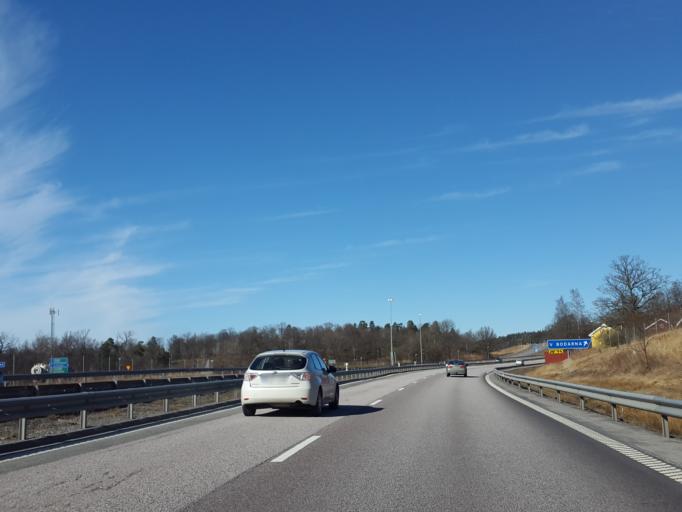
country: SE
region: Vaestra Goetaland
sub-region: Alingsas Kommun
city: Ingared
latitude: 57.8942
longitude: 12.4887
